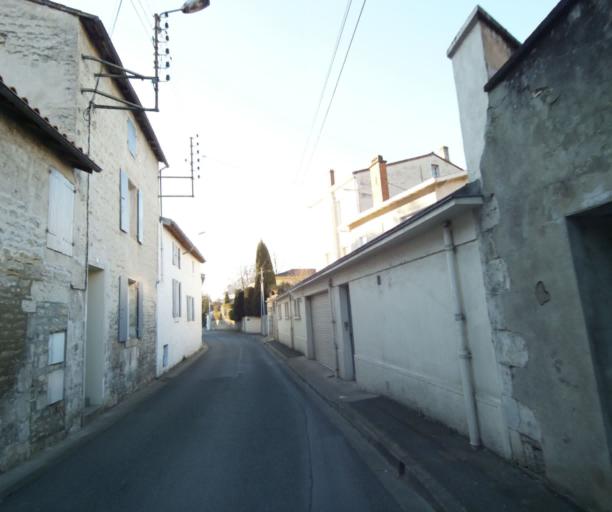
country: FR
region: Poitou-Charentes
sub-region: Departement des Deux-Sevres
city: Niort
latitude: 46.3233
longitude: -0.4723
